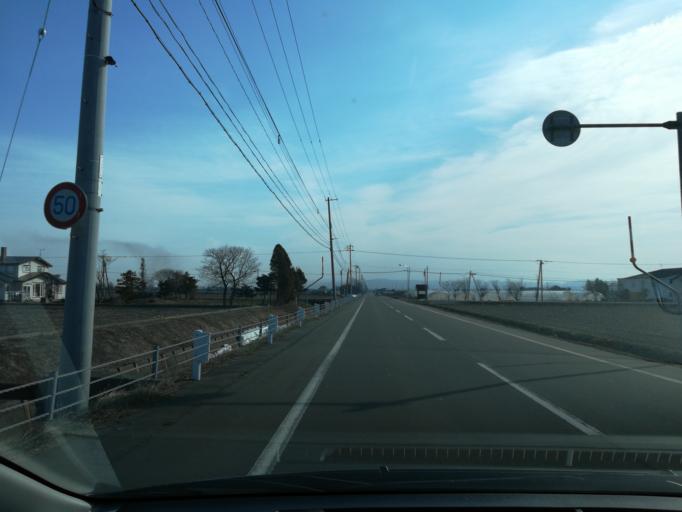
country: JP
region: Hokkaido
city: Iwamizawa
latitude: 43.1799
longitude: 141.6867
